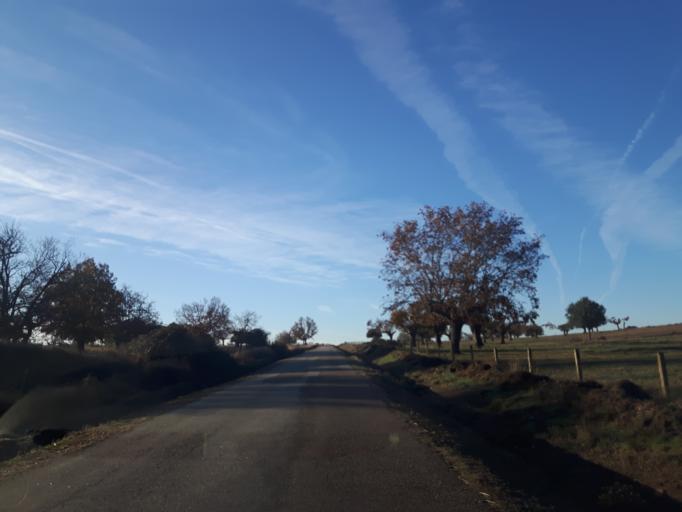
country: ES
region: Castille and Leon
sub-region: Provincia de Salamanca
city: Cerralbo
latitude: 40.9657
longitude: -6.5922
